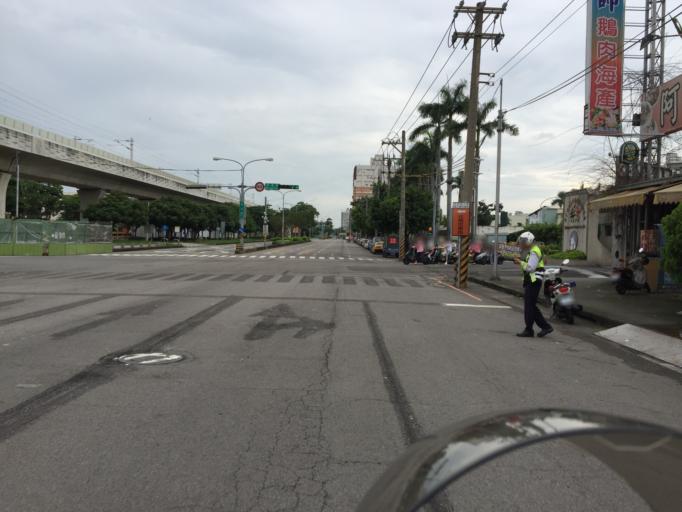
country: TW
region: Taiwan
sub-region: Taichung City
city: Taichung
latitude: 24.1552
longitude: 120.6990
